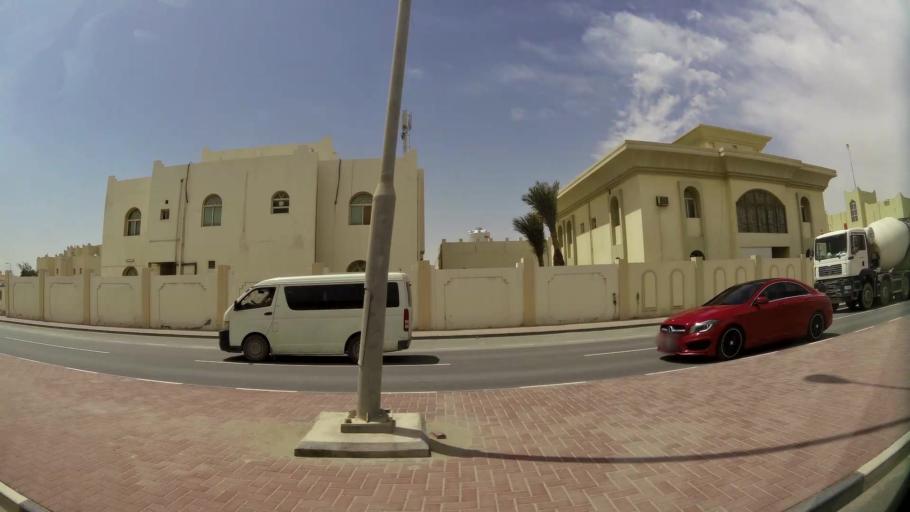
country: QA
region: Baladiyat ar Rayyan
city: Ar Rayyan
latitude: 25.2907
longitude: 51.4151
